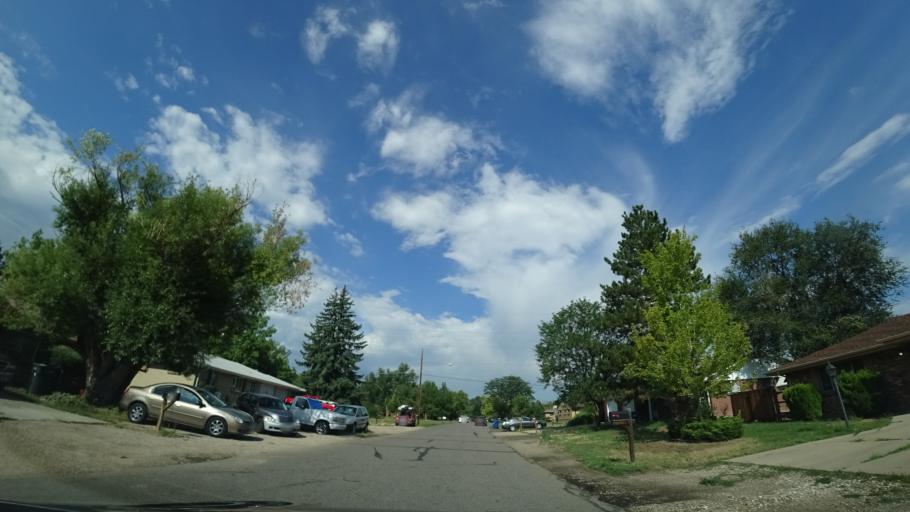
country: US
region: Colorado
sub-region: Jefferson County
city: Lakewood
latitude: 39.7241
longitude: -105.0599
